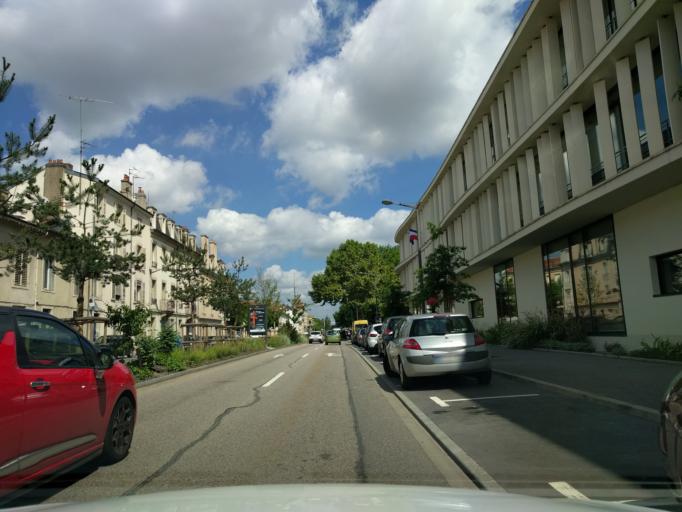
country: FR
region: Lorraine
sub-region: Departement de Meurthe-et-Moselle
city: Nancy
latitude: 48.6847
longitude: 6.1963
